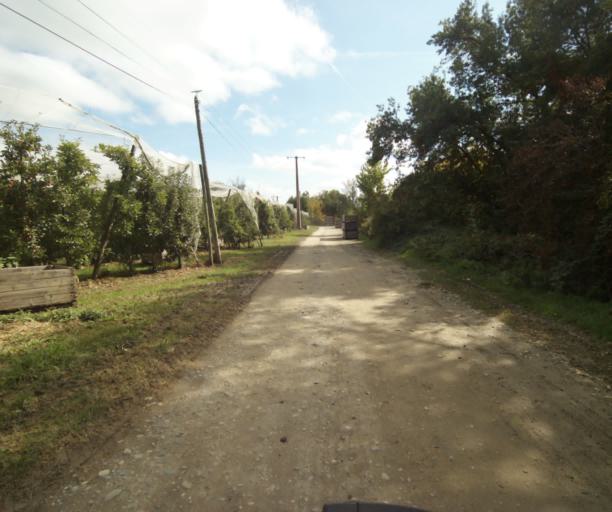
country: FR
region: Midi-Pyrenees
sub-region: Departement du Tarn-et-Garonne
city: Montech
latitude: 43.9511
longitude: 1.1868
